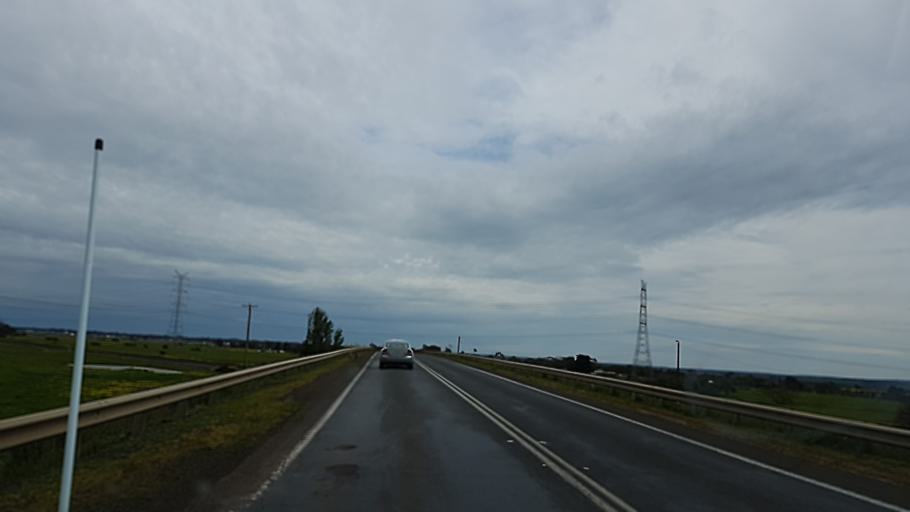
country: AU
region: Victoria
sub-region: Greater Geelong
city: Bell Post Hill
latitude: -38.0759
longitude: 144.2330
